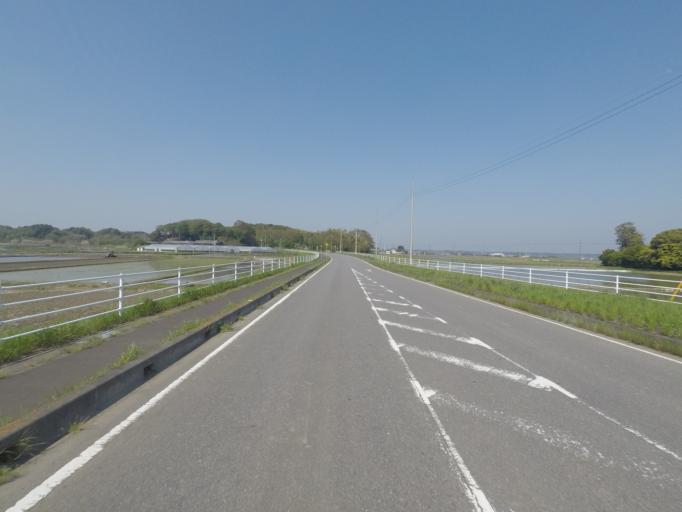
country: JP
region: Ibaraki
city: Inashiki
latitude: 36.0798
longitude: 140.3782
